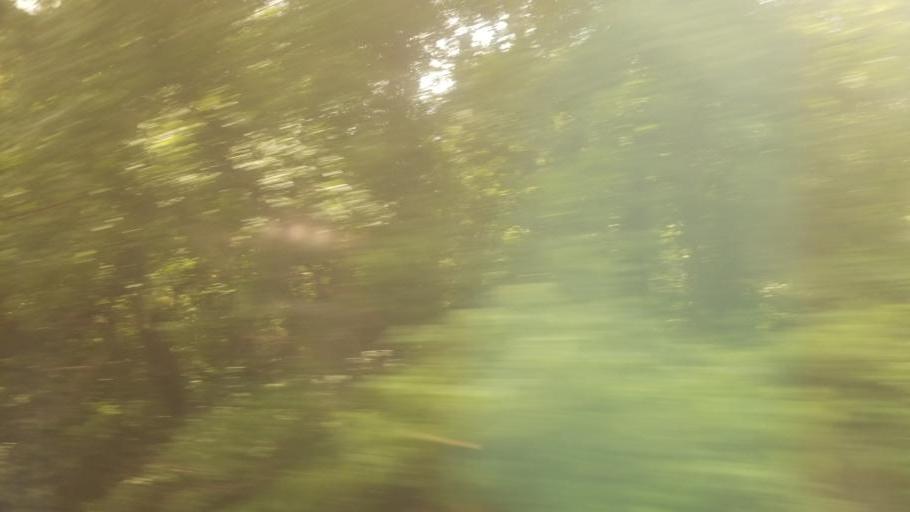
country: US
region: Maryland
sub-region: Frederick County
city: Point of Rocks
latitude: 39.2565
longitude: -77.4959
